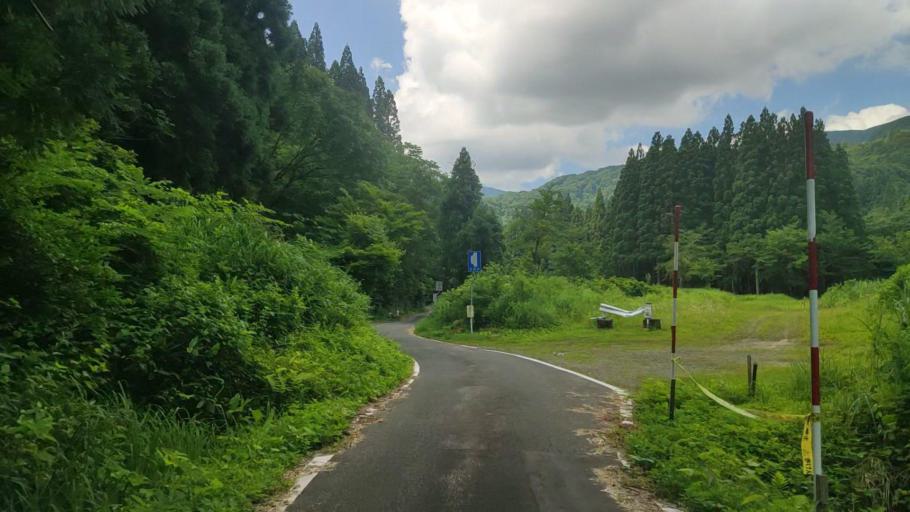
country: JP
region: Fukui
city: Katsuyama
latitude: 36.1962
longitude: 136.5250
